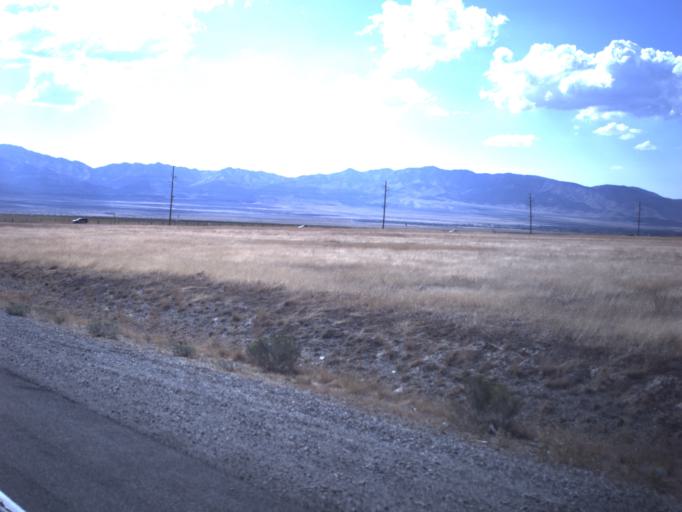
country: US
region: Utah
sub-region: Tooele County
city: Tooele
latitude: 40.5495
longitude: -112.3395
